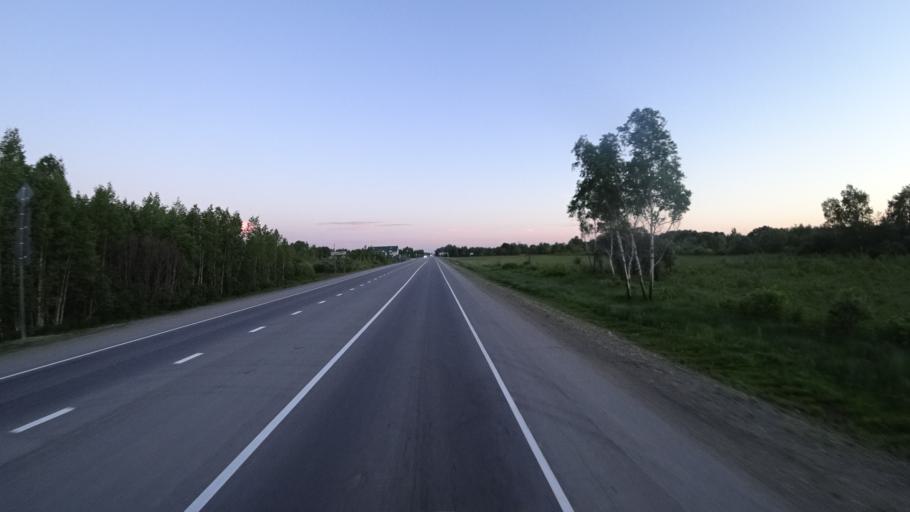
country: RU
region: Khabarovsk Krai
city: Khor
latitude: 47.8452
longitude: 134.9578
